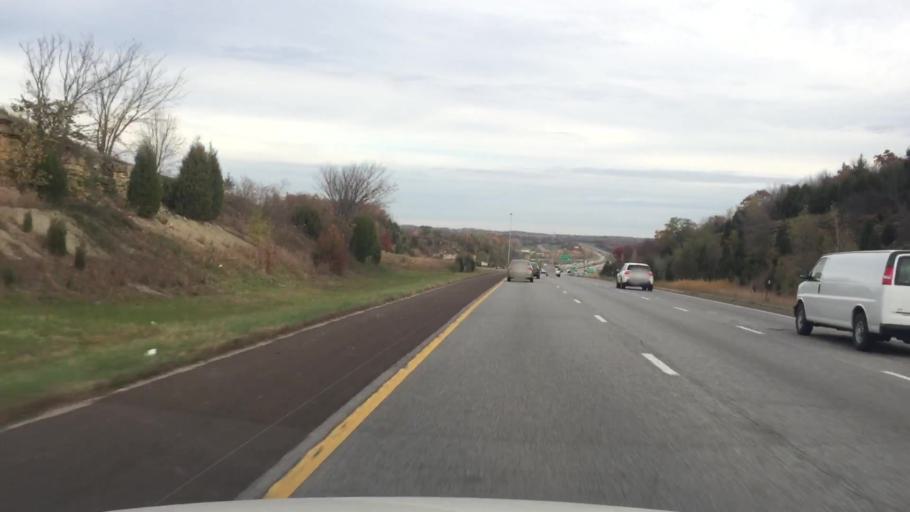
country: US
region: Kansas
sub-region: Wyandotte County
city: Edwardsville
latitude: 39.0339
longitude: -94.7876
